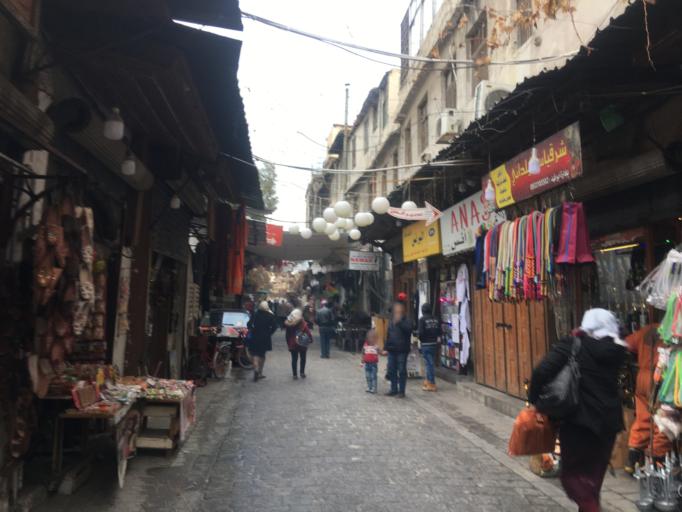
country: SY
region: Dimashq
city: Damascus
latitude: 33.5117
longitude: 36.3092
